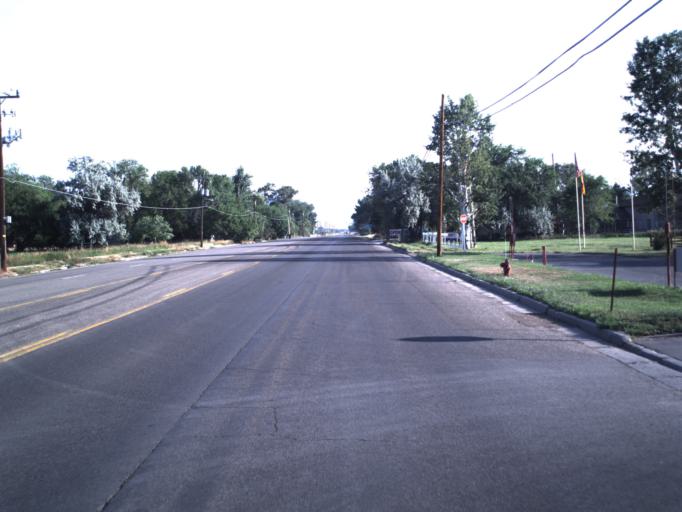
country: US
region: Utah
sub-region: Uintah County
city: Vernal
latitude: 40.4693
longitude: -109.5287
